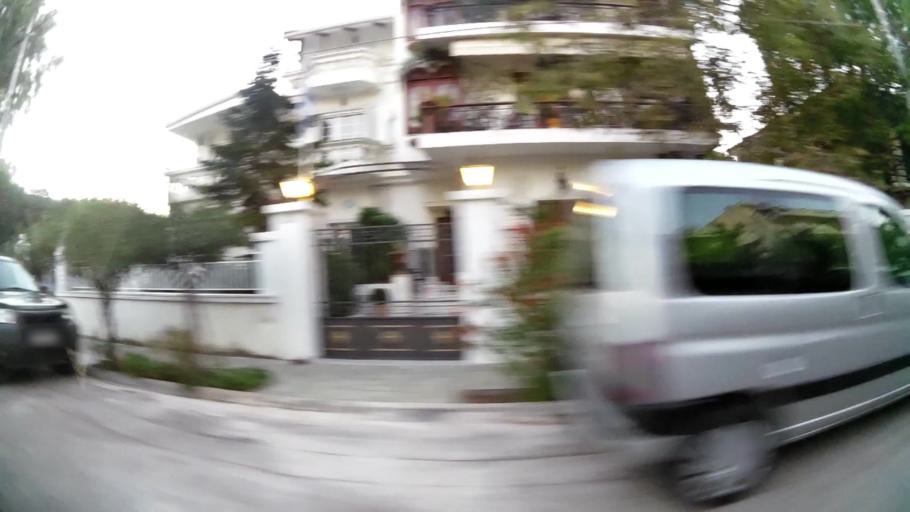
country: GR
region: Attica
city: Pefki
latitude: 38.0653
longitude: 23.8018
